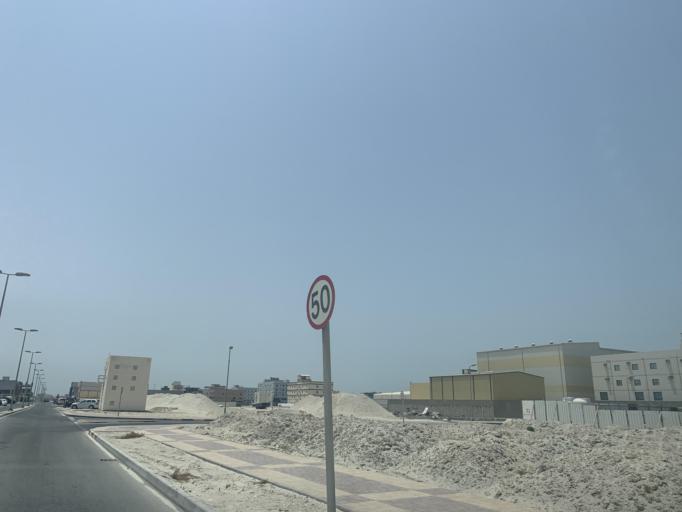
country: BH
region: Muharraq
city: Al Hadd
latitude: 26.2564
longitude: 50.6715
